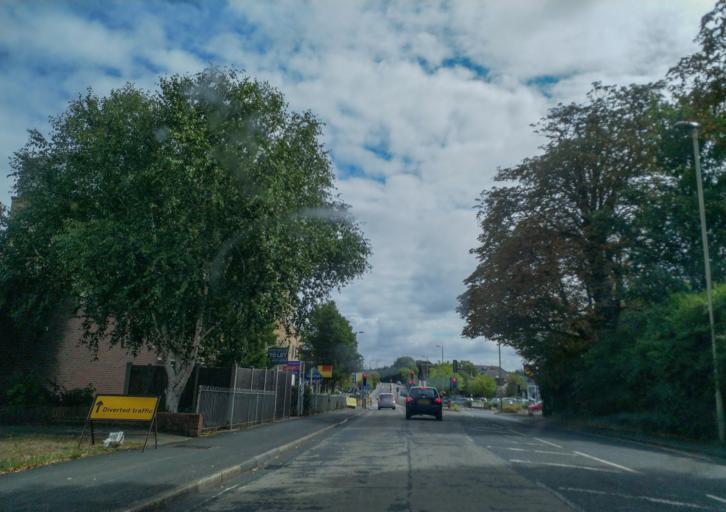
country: GB
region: England
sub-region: Bracknell Forest
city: Sandhurst
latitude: 51.3306
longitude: -0.7809
